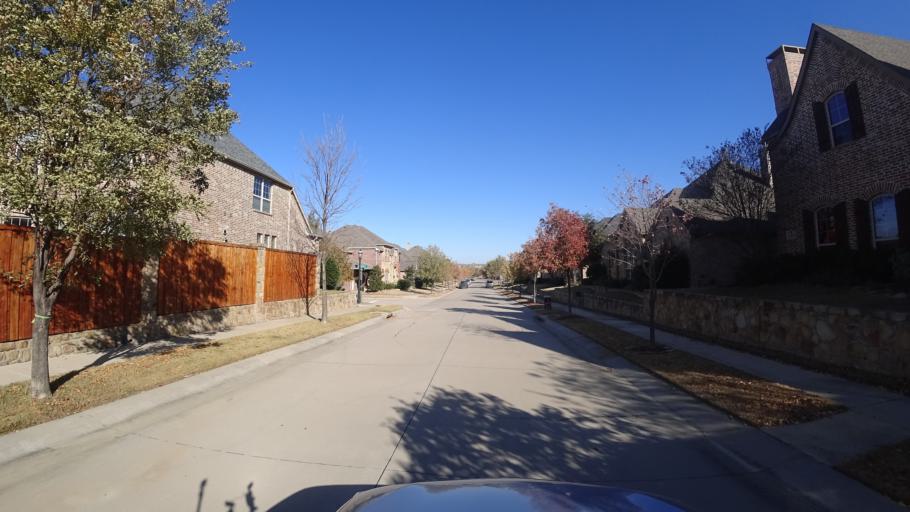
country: US
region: Texas
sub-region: Denton County
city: The Colony
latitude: 33.0417
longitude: -96.9192
